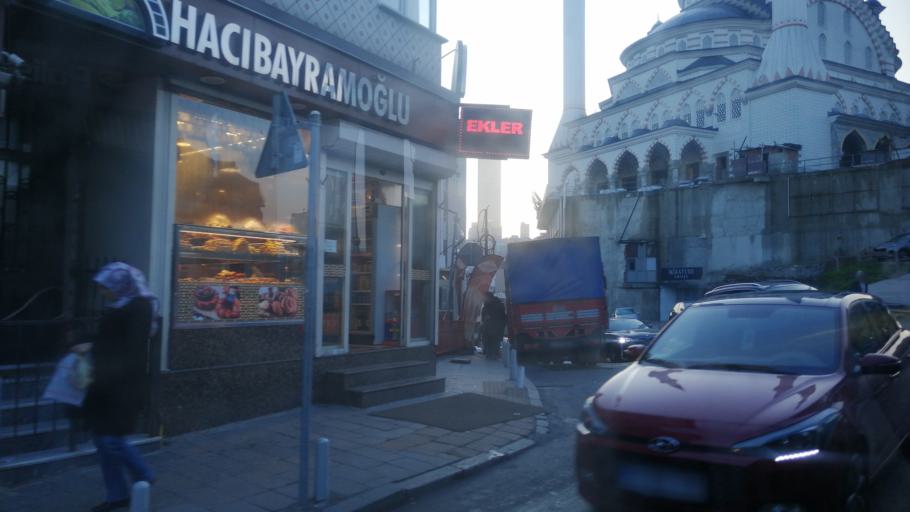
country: TR
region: Istanbul
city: Sisli
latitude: 41.0855
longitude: 28.9869
